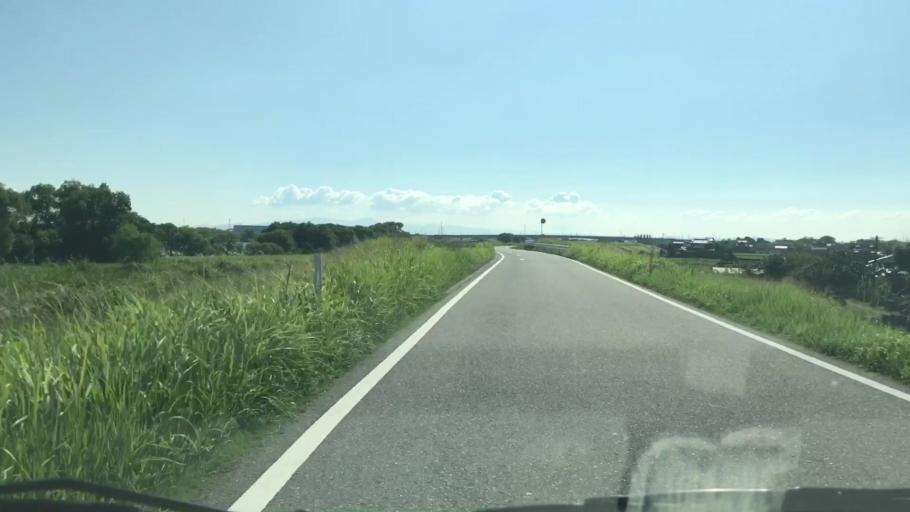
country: JP
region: Saga Prefecture
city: Kanzakimachi-kanzaki
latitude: 33.2758
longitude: 130.4429
